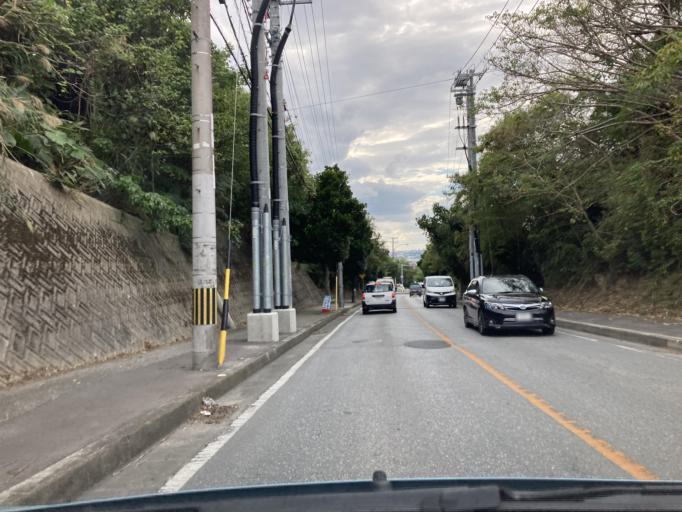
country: JP
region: Okinawa
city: Katsuren-haebaru
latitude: 26.3329
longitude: 127.8771
